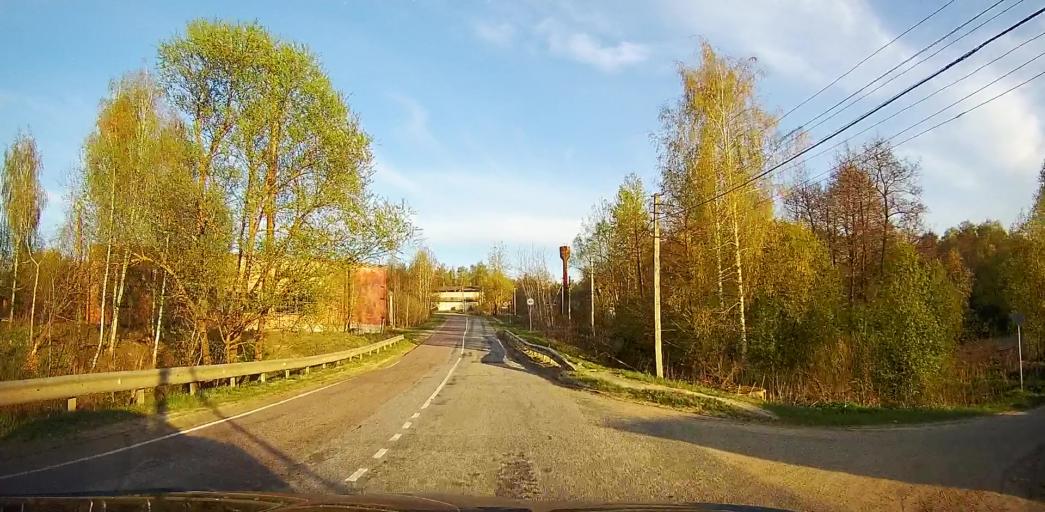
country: RU
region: Moskovskaya
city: Meshcherino
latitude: 55.2300
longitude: 38.3690
